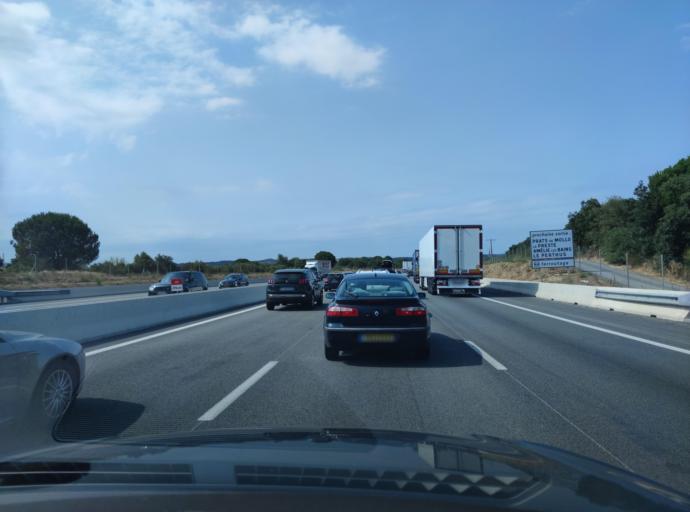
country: FR
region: Languedoc-Roussillon
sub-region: Departement des Pyrenees-Orientales
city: Maureillas-las-Illas
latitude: 42.5026
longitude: 2.8183
